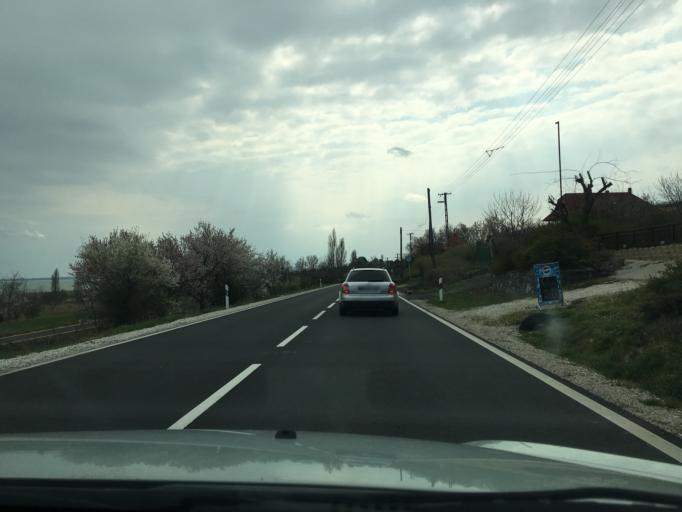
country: HU
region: Zala
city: Vonyarcvashegy
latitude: 46.7776
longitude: 17.3662
